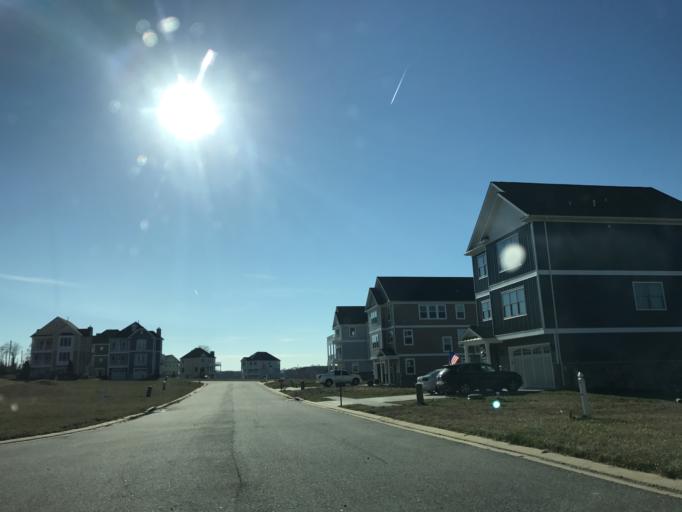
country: US
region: Maryland
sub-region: Harford County
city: Riverside
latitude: 39.4424
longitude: -76.2343
